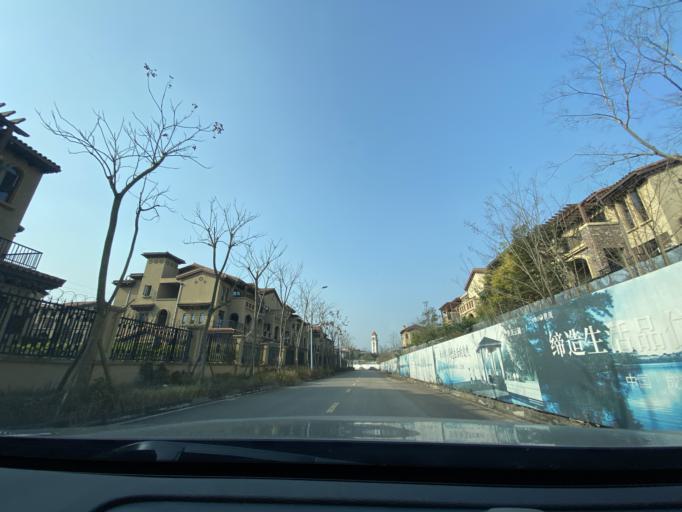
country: CN
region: Sichuan
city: Wenlin
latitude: 30.2535
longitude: 104.2455
